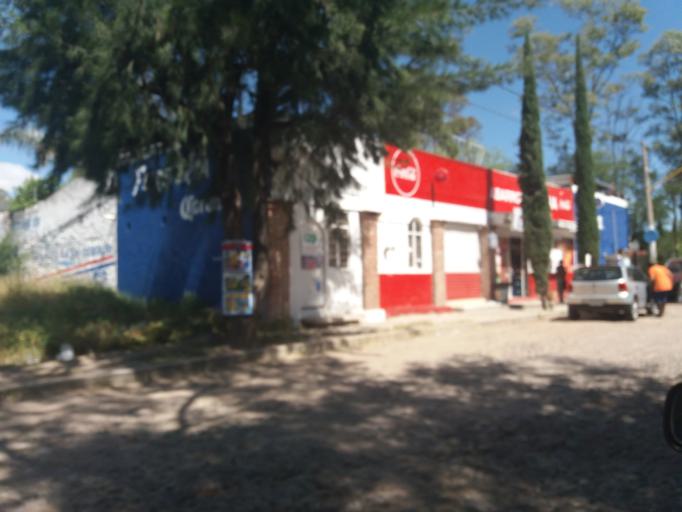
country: MX
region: Aguascalientes
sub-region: Aguascalientes
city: San Sebastian [Fraccionamiento]
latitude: 21.7905
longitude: -102.2810
